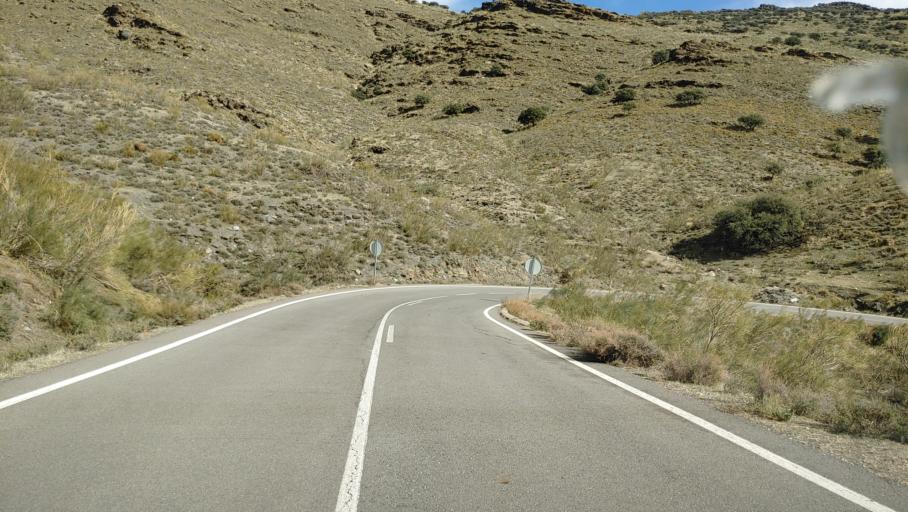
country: ES
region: Andalusia
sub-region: Provincia de Almeria
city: Ohanes
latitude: 37.0740
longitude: -2.7281
